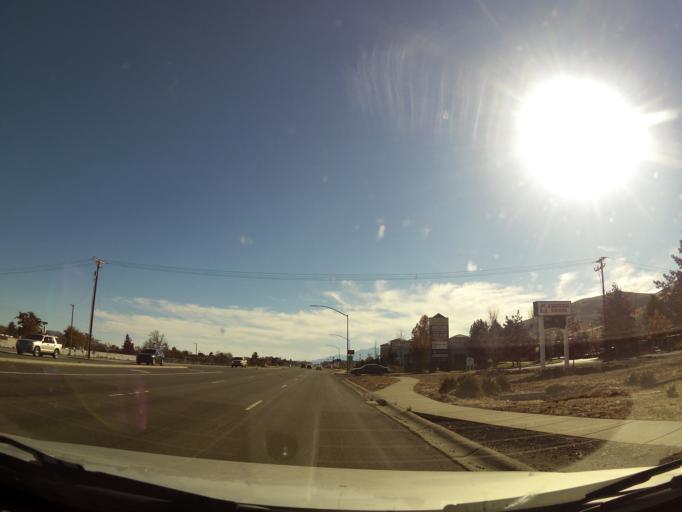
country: US
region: Nevada
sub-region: Carson City
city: Carson City
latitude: 39.1471
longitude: -119.7675
